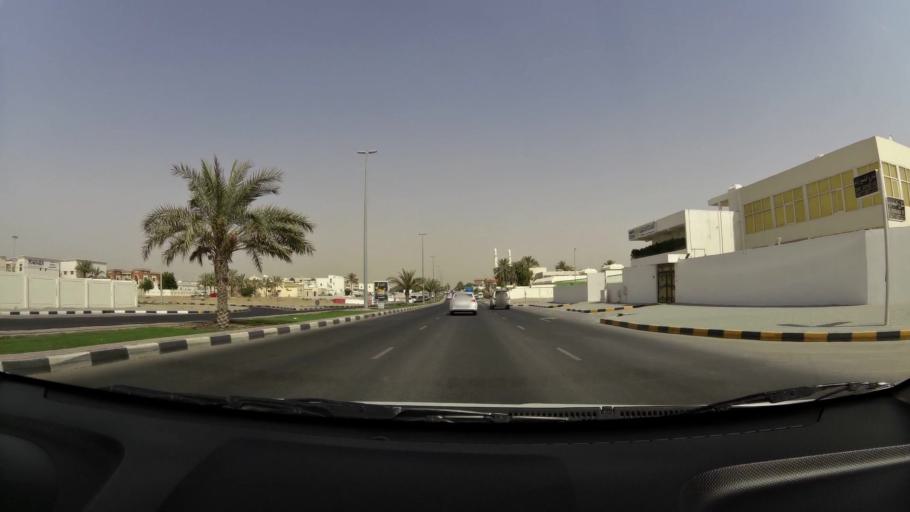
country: AE
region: Ash Shariqah
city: Sharjah
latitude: 25.3427
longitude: 55.4256
